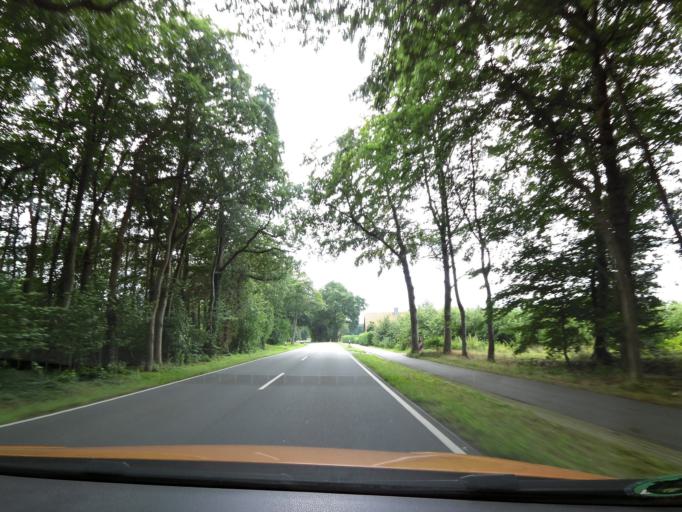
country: DE
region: Lower Saxony
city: Gross Ippener
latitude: 52.9897
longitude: 8.6158
